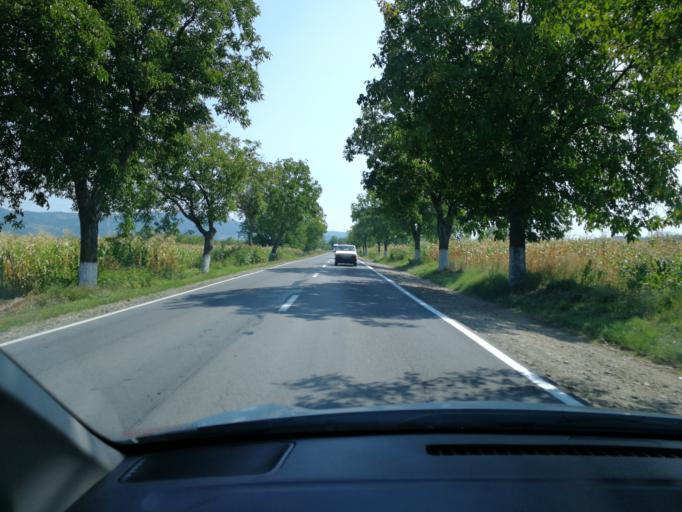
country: RO
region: Prahova
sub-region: Comuna Izvoarele
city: Homoraciu
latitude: 45.2459
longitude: 26.0245
